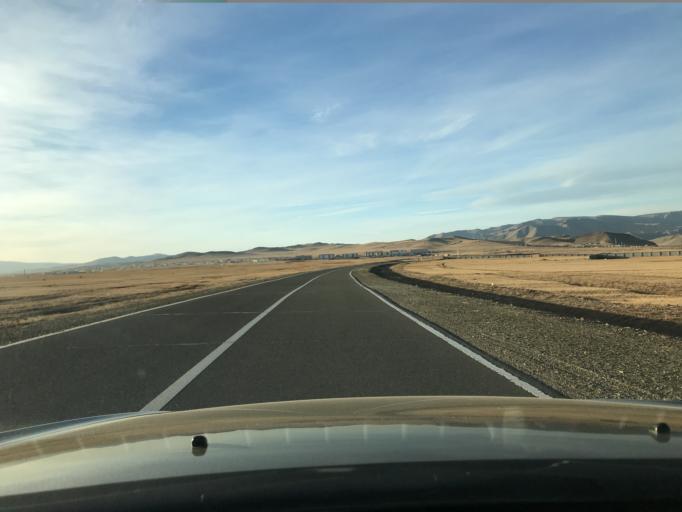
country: MN
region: Central Aimak
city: Arhust
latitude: 47.7690
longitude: 107.4171
